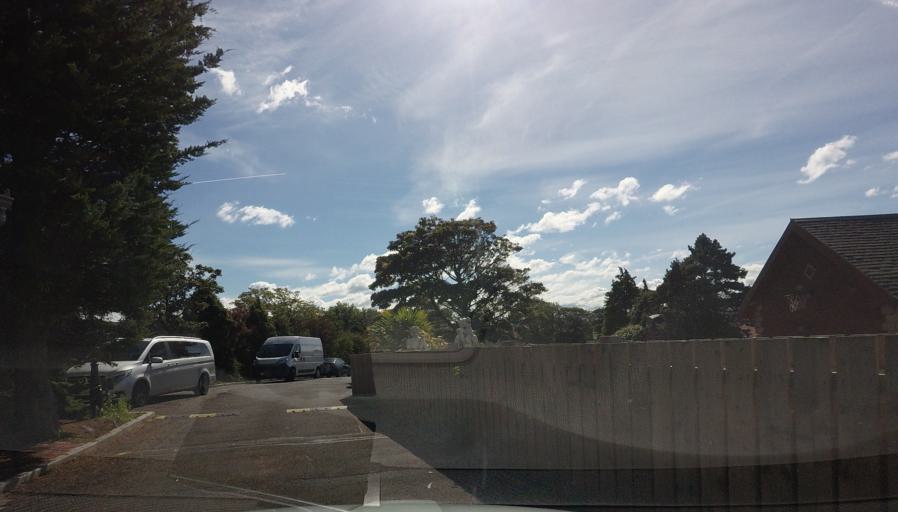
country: GB
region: Scotland
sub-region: East Lothian
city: East Linton
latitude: 55.9759
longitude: -2.7077
